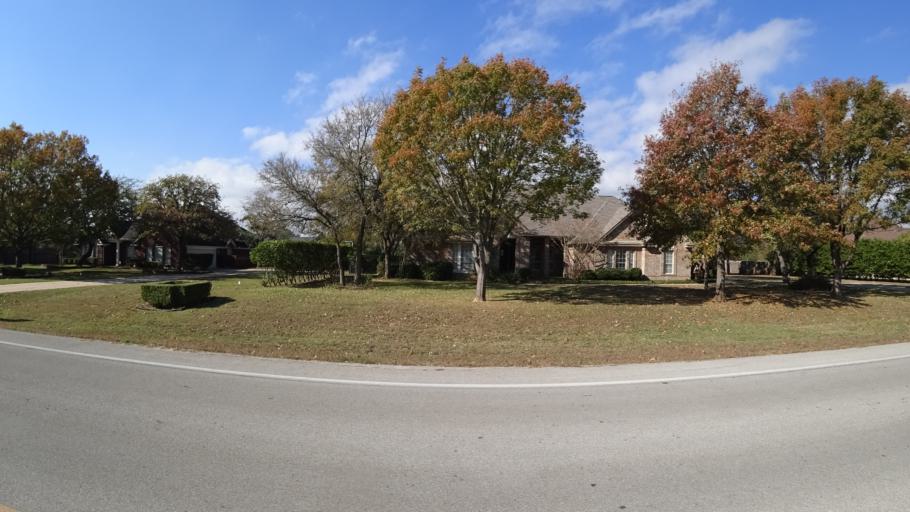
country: US
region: Texas
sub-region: Travis County
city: Shady Hollow
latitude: 30.1599
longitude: -97.8734
